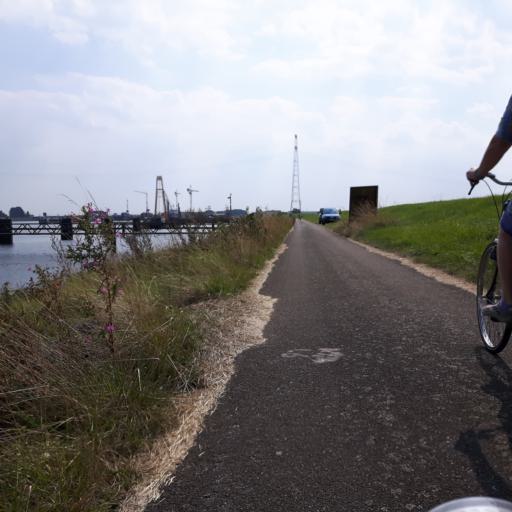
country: NL
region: Zeeland
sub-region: Gemeente Reimerswaal
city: Yerseke
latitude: 51.4647
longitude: 4.0044
